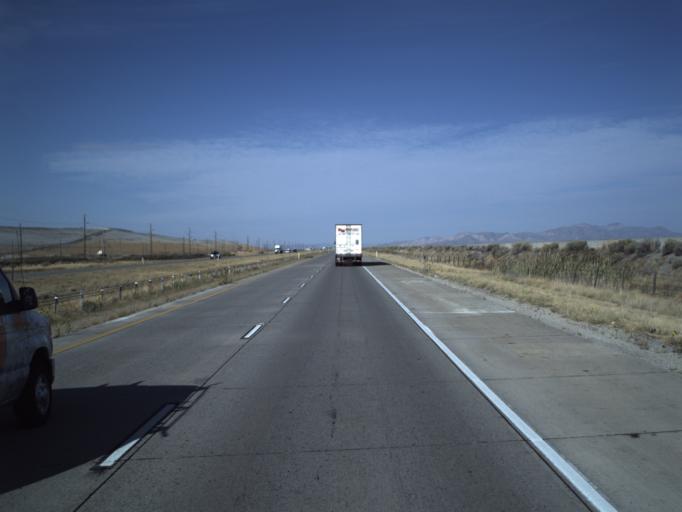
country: US
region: Utah
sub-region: Salt Lake County
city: Magna
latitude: 40.7710
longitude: -112.1114
